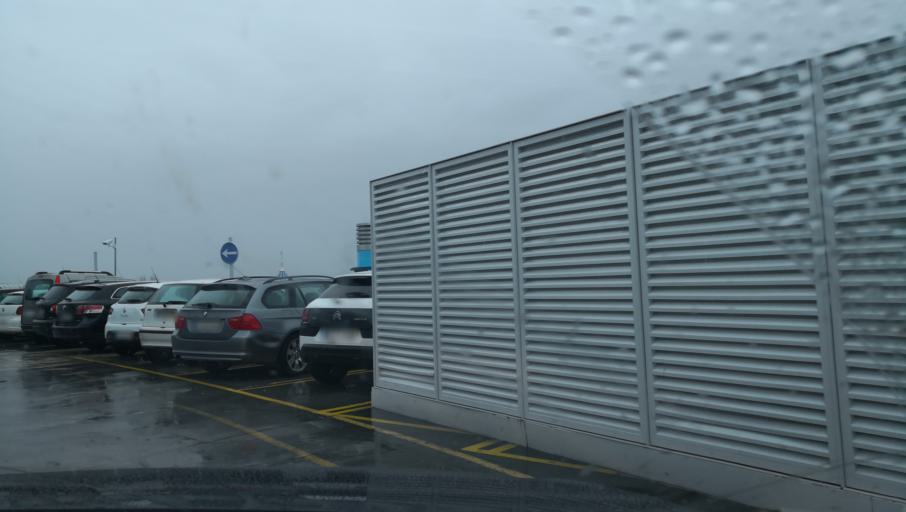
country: PT
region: Porto
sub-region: Vila Nova de Gaia
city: Vila Nova de Gaia
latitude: 41.1174
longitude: -8.6220
